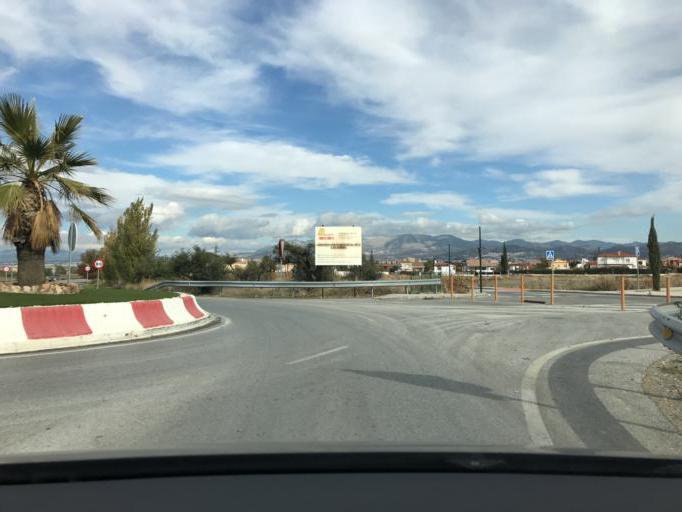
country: ES
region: Andalusia
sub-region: Provincia de Granada
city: Churriana de la Vega
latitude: 37.1404
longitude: -3.6592
